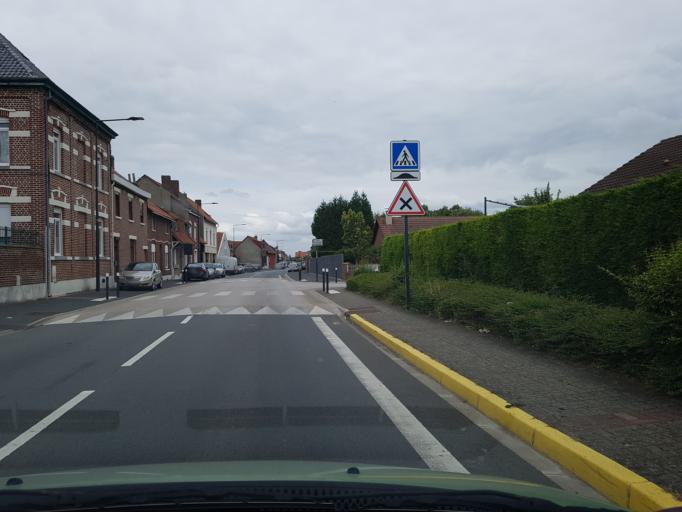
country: FR
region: Nord-Pas-de-Calais
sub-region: Departement du Pas-de-Calais
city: Hulluch
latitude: 50.4851
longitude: 2.8197
